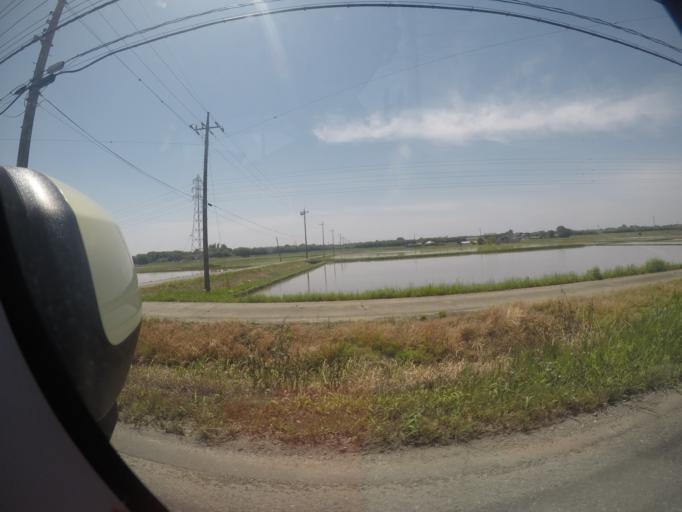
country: JP
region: Ibaraki
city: Tsukuba
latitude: 36.2140
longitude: 140.0688
